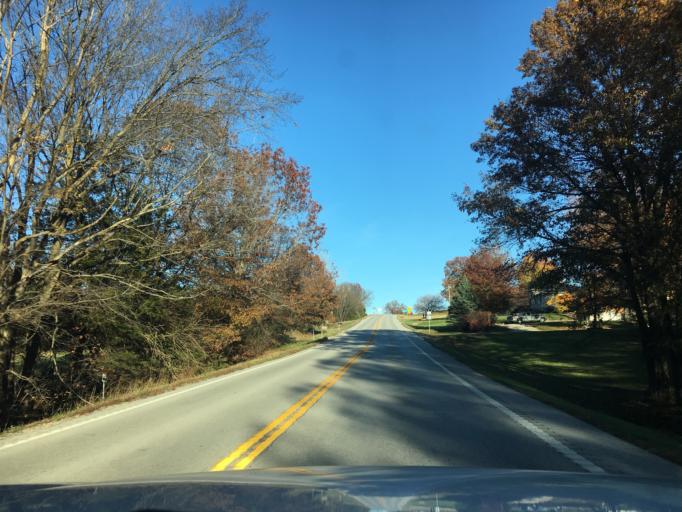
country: US
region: Missouri
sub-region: Franklin County
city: New Haven
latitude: 38.5991
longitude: -91.2445
